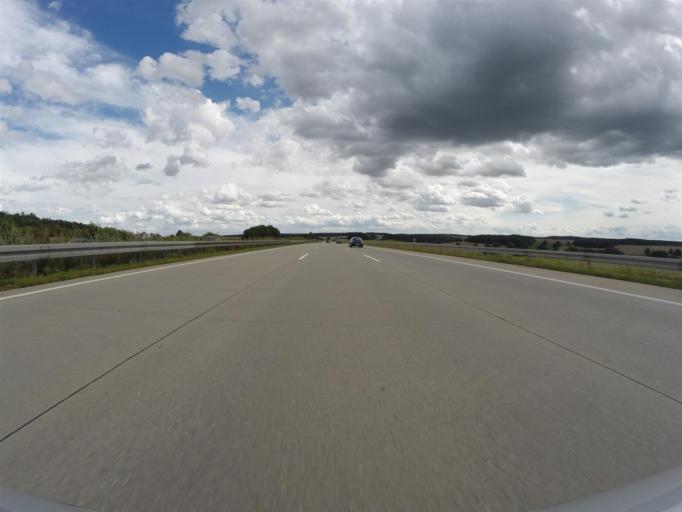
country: DE
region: Thuringia
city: Eineborn
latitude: 50.8354
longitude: 11.8726
